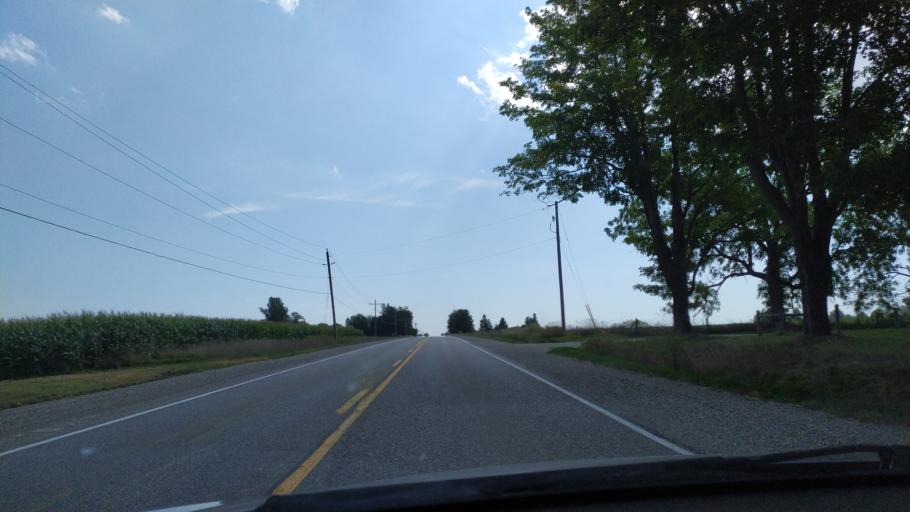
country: CA
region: Ontario
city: Ingersoll
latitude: 43.1277
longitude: -80.8873
